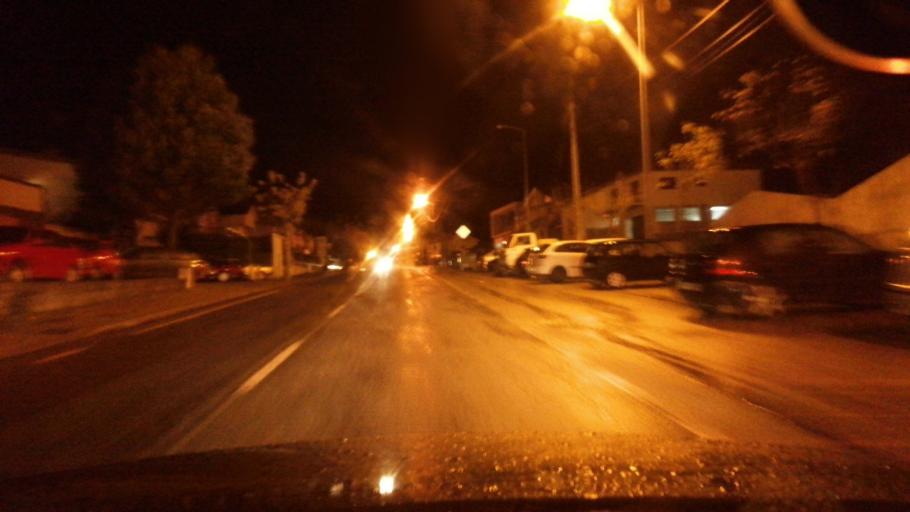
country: PT
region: Viseu
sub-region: Moimenta da Beira
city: Moimenta da Beira
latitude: 40.9707
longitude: -7.6066
